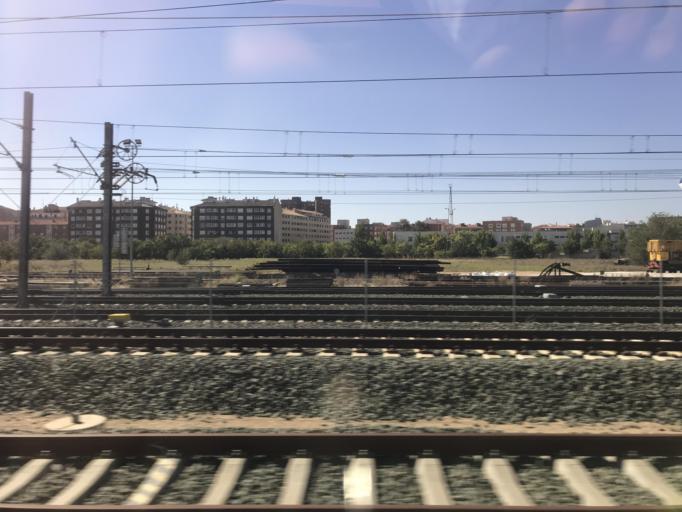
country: ES
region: Castille-La Mancha
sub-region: Provincia de Albacete
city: Albacete
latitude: 39.0034
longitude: -1.8505
